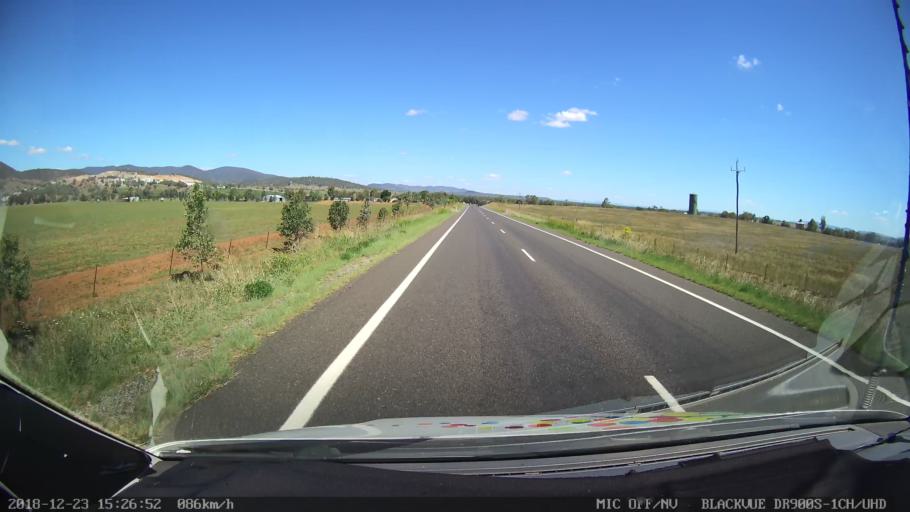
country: AU
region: New South Wales
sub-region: Tamworth Municipality
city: East Tamworth
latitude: -30.9218
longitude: 150.8416
